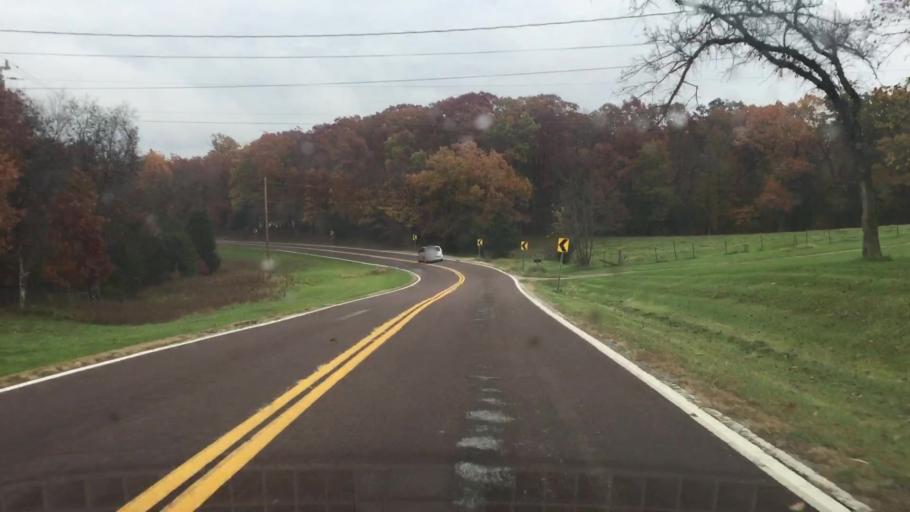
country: US
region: Missouri
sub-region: Callaway County
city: Fulton
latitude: 38.7799
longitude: -91.8312
